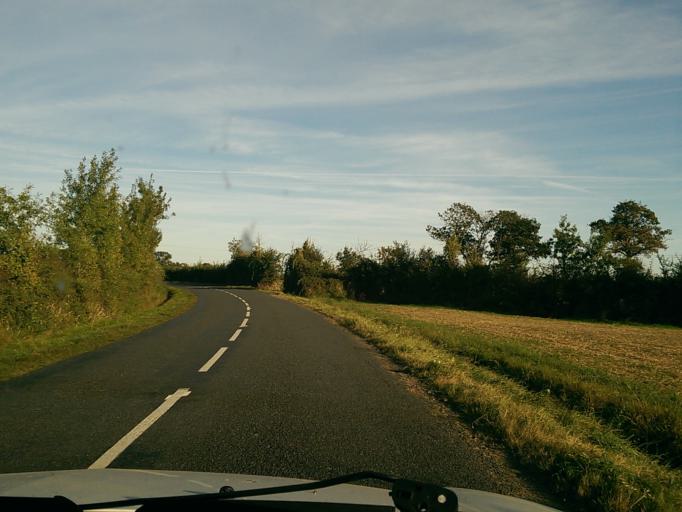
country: FR
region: Pays de la Loire
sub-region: Departement de Maine-et-Loire
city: Vihiers
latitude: 47.2078
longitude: -0.5428
